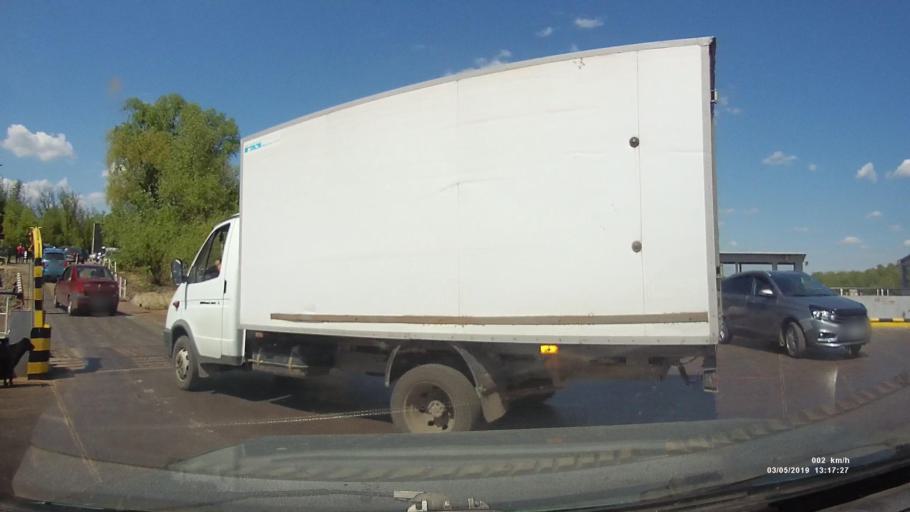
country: RU
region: Rostov
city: Semikarakorsk
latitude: 47.5298
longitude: 40.7513
